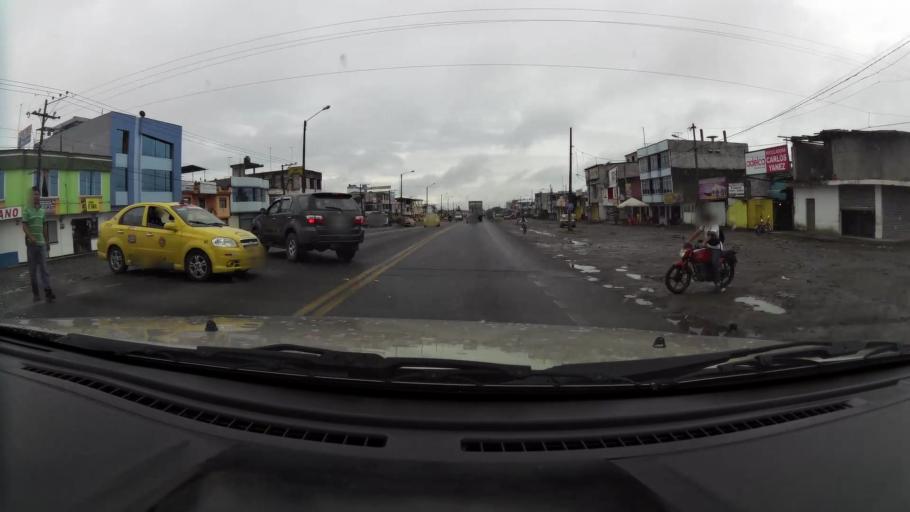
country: EC
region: Santo Domingo de los Tsachilas
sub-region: Canton Santo Domingo de los Colorados
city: Santo Domingo de los Colorados
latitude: -0.2377
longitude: -79.1766
